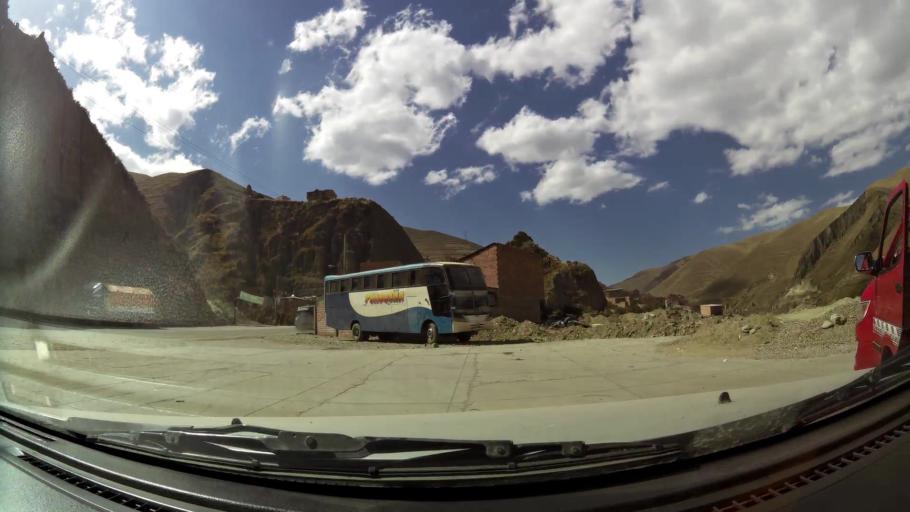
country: BO
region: La Paz
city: La Paz
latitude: -16.4559
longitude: -68.1001
